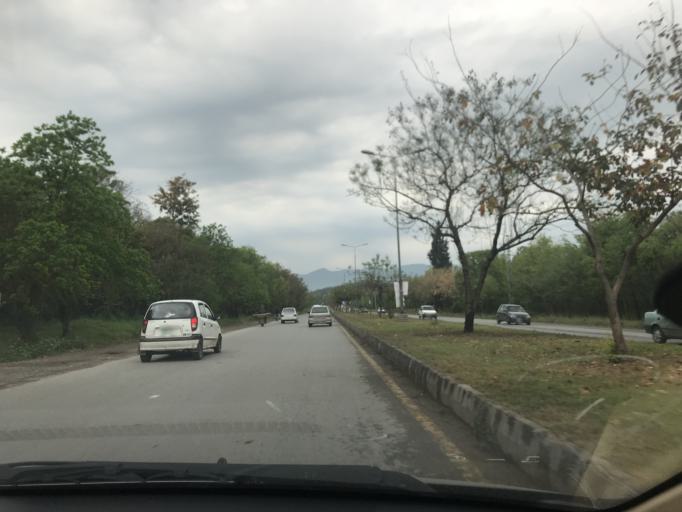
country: PK
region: Islamabad
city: Islamabad
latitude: 33.6818
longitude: 73.1377
